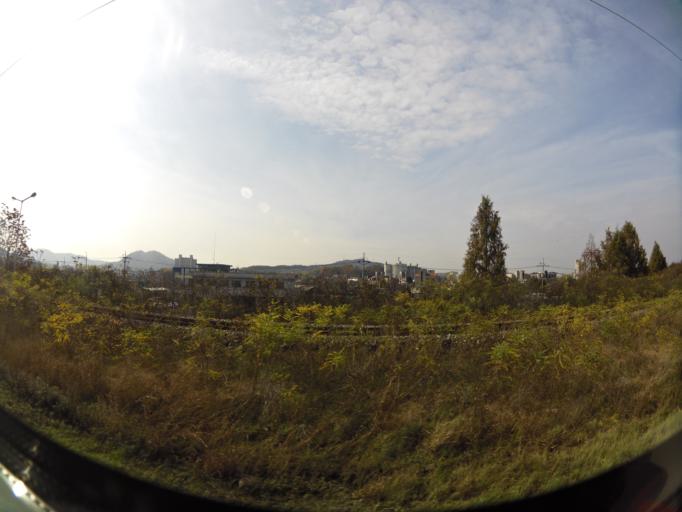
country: KR
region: Daejeon
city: Sintansin
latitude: 36.5287
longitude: 127.3731
